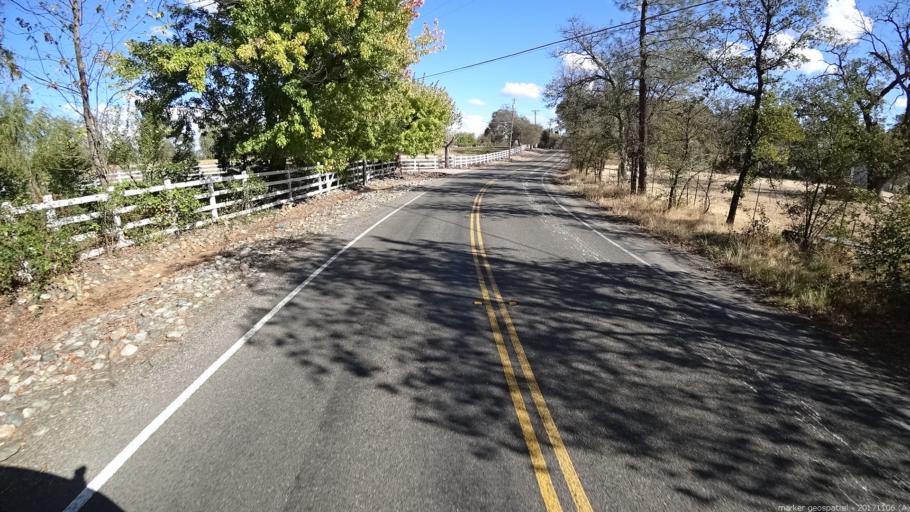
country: US
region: California
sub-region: Shasta County
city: Palo Cedro
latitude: 40.5927
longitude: -122.2430
